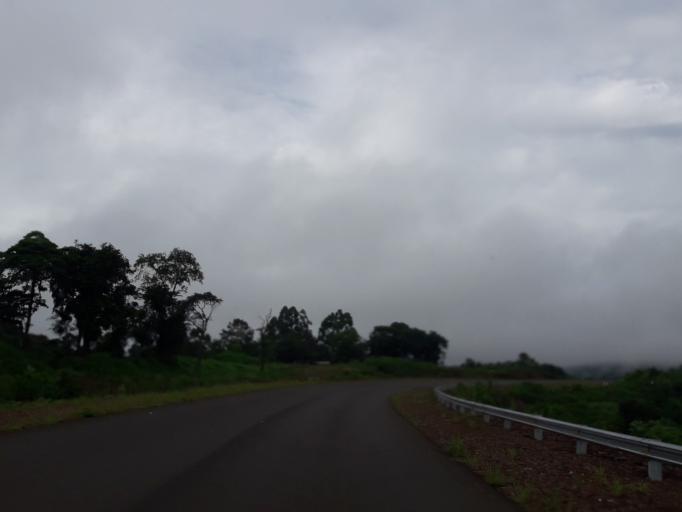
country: AR
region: Misiones
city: Bernardo de Irigoyen
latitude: -26.4180
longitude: -53.8245
